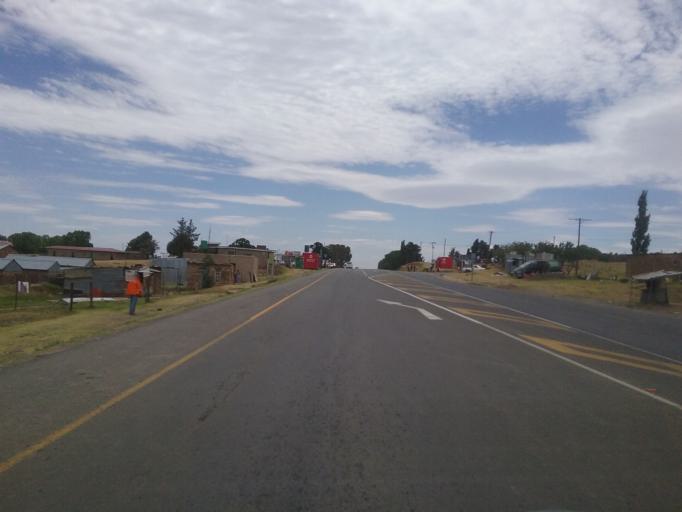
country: LS
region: Maseru
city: Maseru
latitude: -29.4894
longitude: 27.5272
